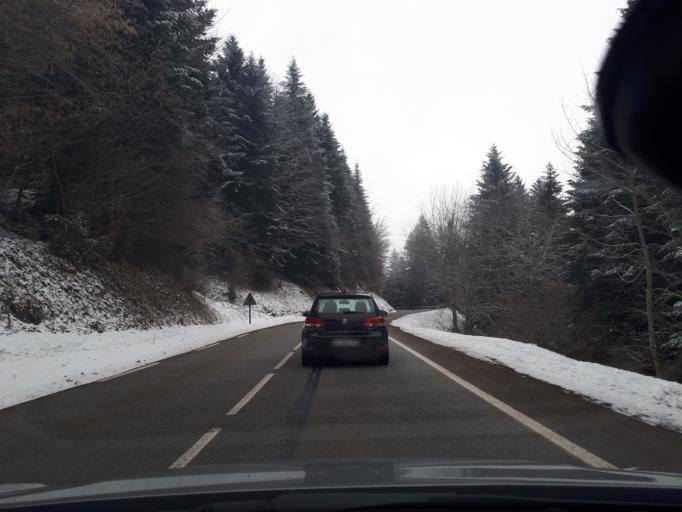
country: FR
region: Rhone-Alpes
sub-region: Departement de l'Isere
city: Vaulnaveys-le-Bas
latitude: 45.1088
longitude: 5.8428
